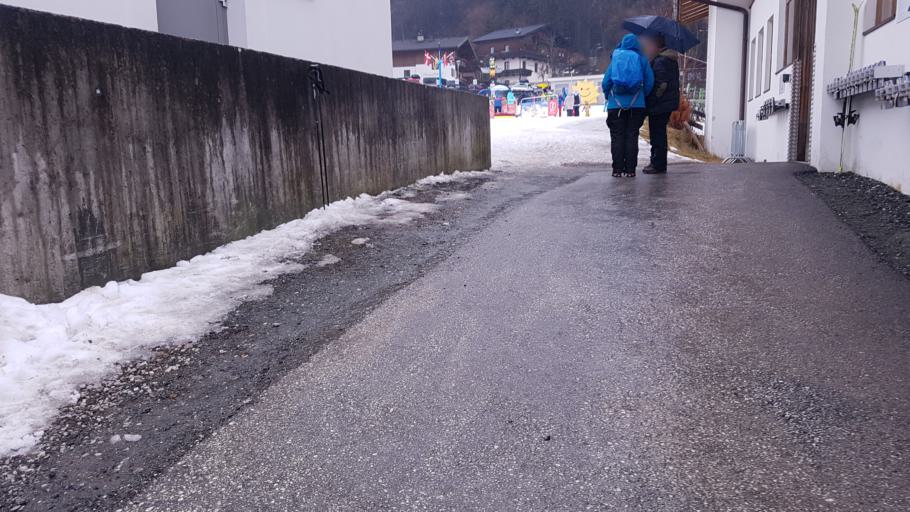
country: AT
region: Salzburg
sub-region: Politischer Bezirk Zell am See
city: Neukirchen am Grossvenediger
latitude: 47.2542
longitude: 12.2807
